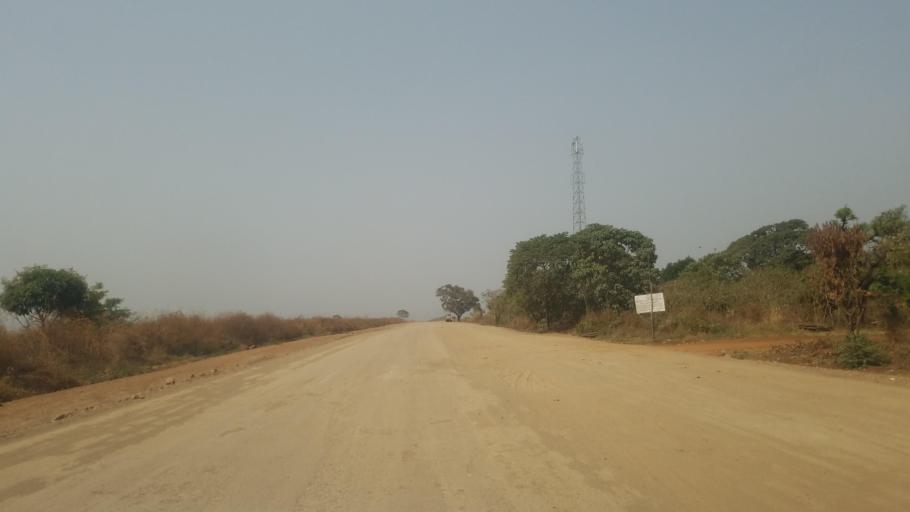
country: ET
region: Amhara
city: Bure
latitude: 10.8965
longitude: 36.4621
